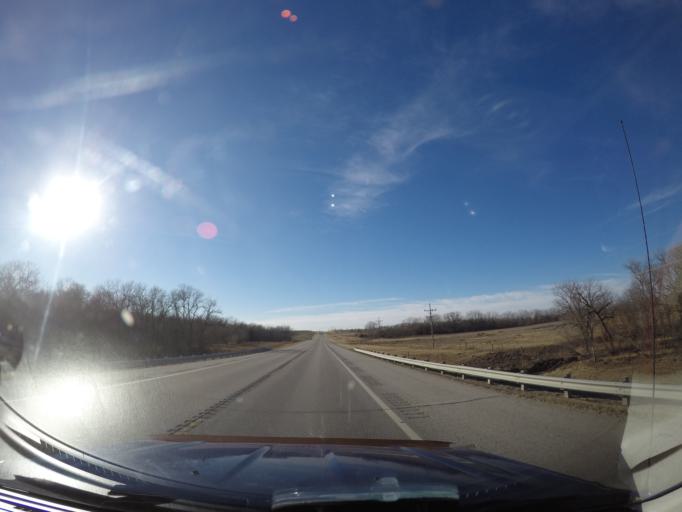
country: US
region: Kansas
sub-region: Marion County
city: Hillsboro
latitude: 38.3624
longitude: -97.3212
